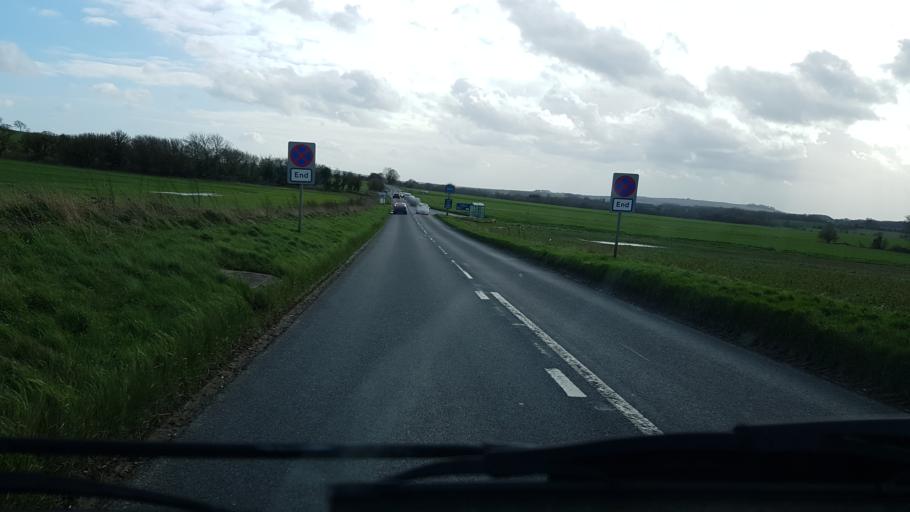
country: GB
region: England
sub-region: Wiltshire
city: Avebury
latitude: 51.4718
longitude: -1.8465
